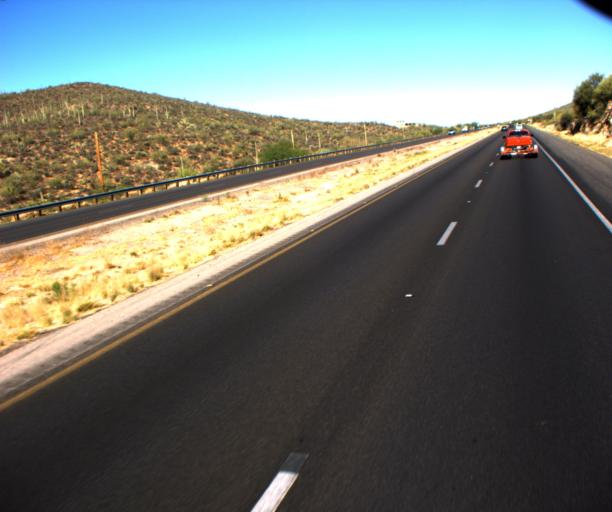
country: US
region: Arizona
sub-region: Pima County
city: Drexel Heights
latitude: 32.1774
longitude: -111.0385
